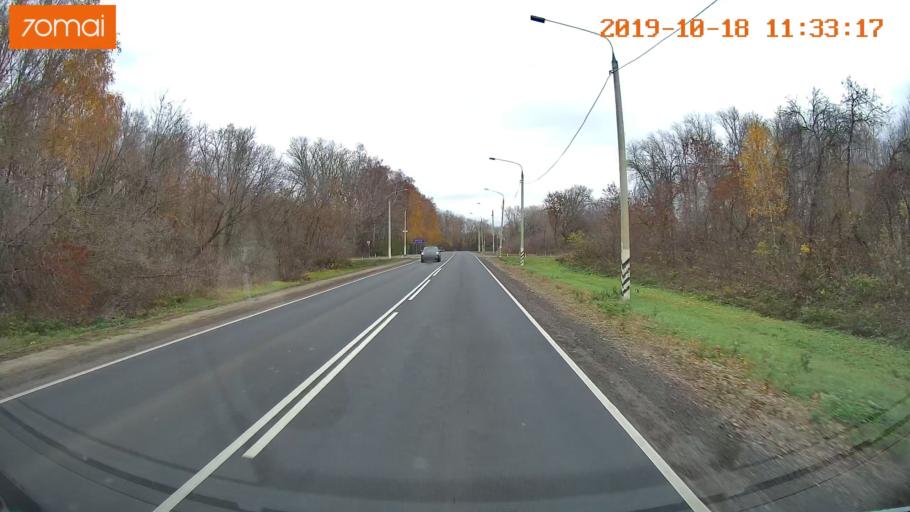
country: RU
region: Rjazan
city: Oktyabr'skiy
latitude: 54.1415
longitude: 38.7359
